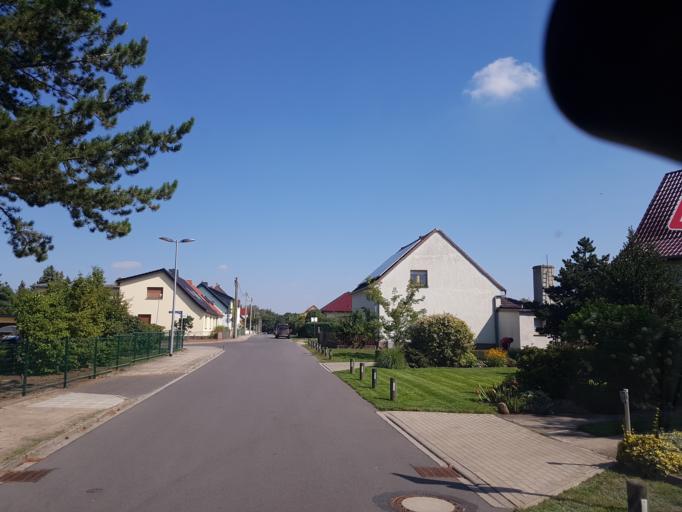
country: DE
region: Brandenburg
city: Elsterwerda
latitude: 51.4928
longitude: 13.5027
